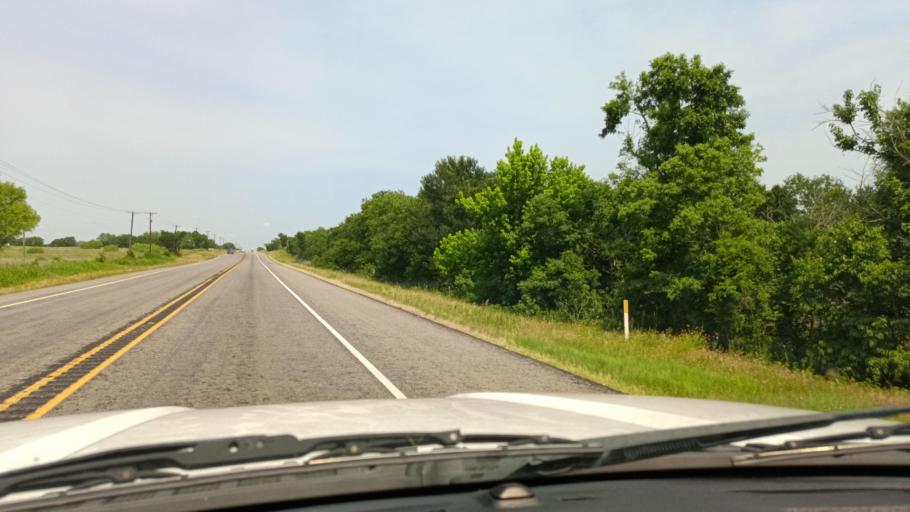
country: US
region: Texas
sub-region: Milam County
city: Cameron
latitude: 30.8488
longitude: -97.0634
